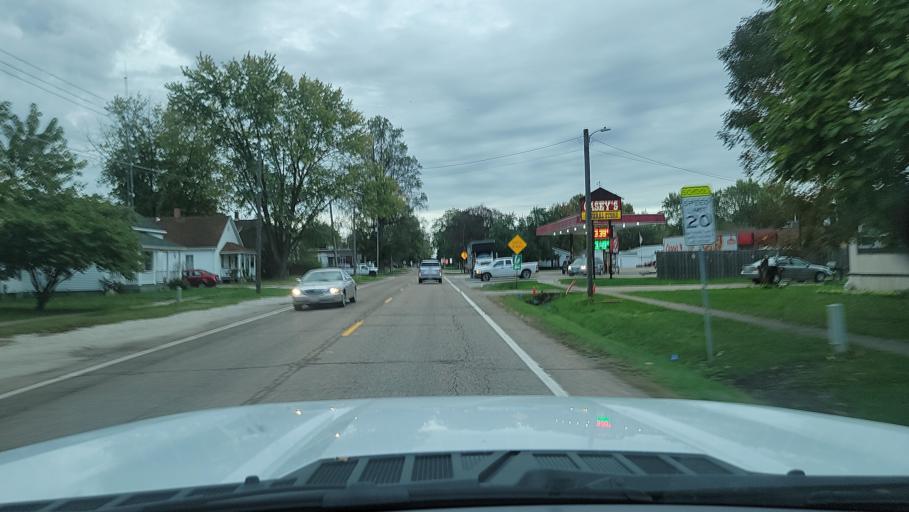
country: US
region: Illinois
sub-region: Schuyler County
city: Rushville
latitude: 40.1176
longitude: -90.5665
